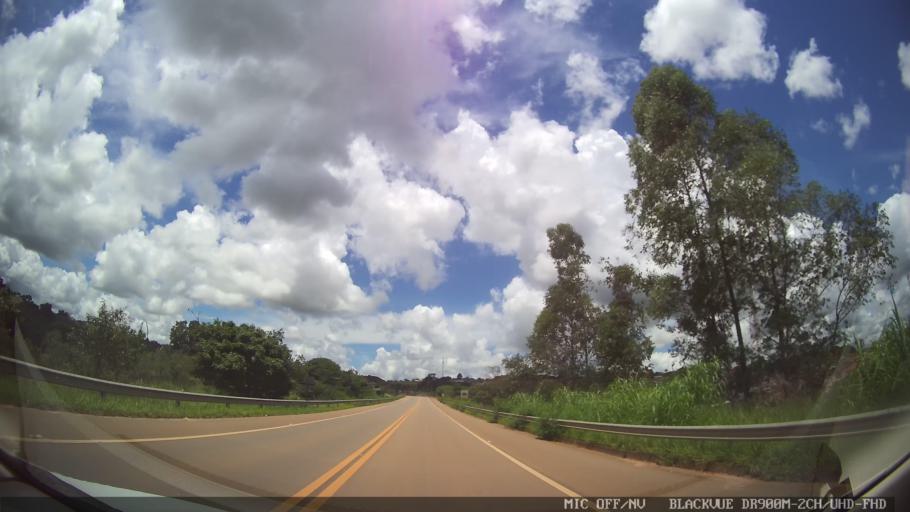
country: BR
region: Sao Paulo
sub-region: Amparo
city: Amparo
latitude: -22.8123
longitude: -46.6930
